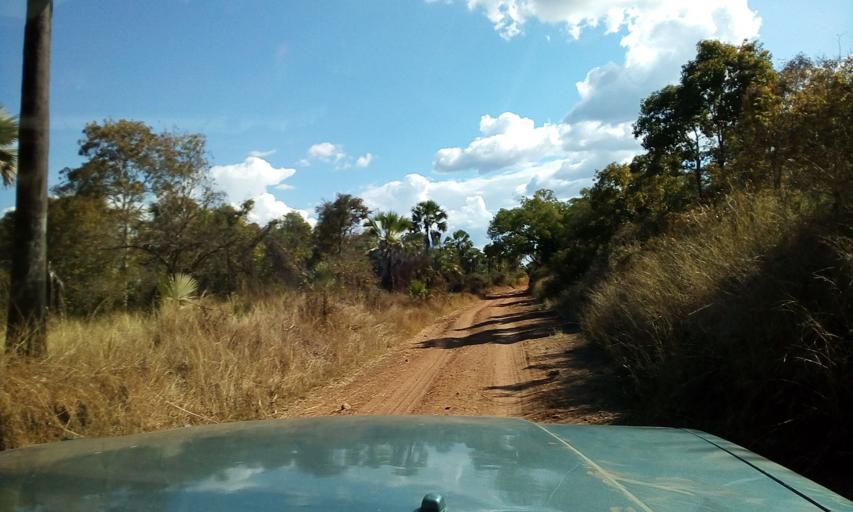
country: MG
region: Boeny
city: Mahajanga
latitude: -16.0599
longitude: 45.7981
